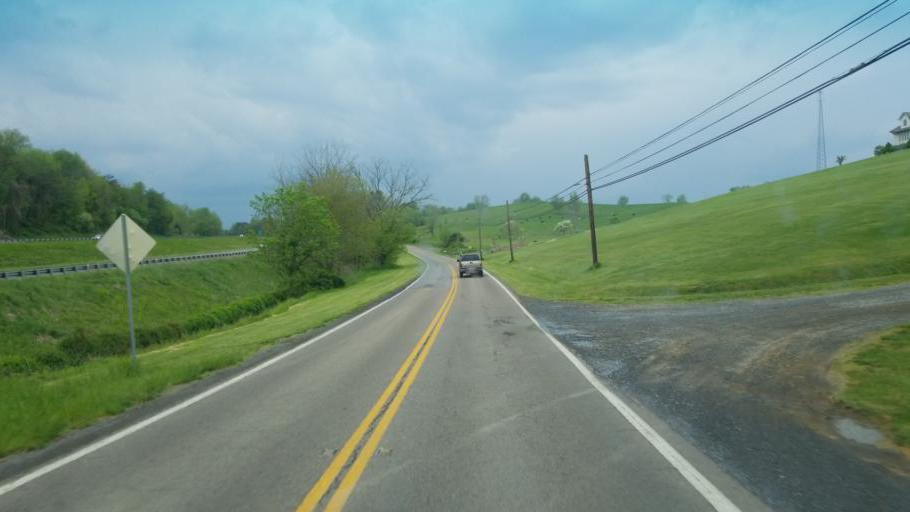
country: US
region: Virginia
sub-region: Smyth County
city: Chilhowie
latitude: 36.7888
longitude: -81.7054
